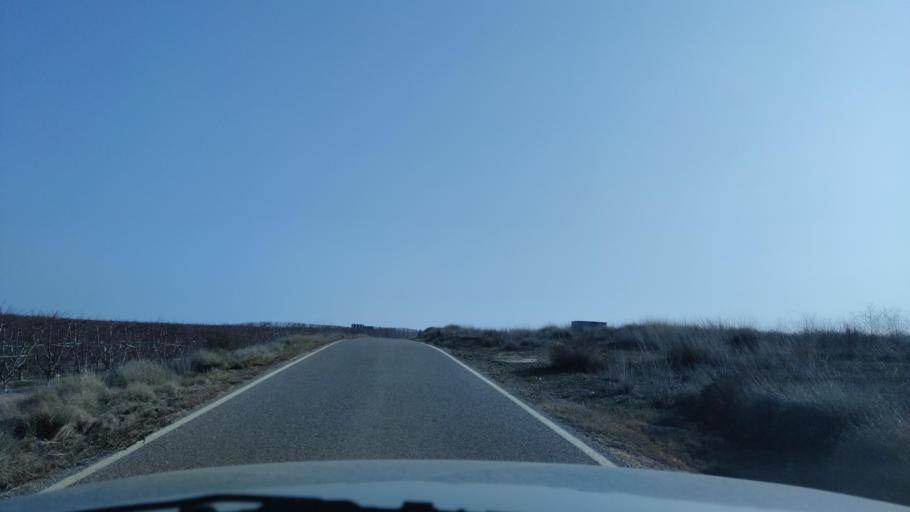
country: ES
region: Catalonia
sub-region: Provincia de Lleida
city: Sunyer
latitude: 41.5300
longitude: 0.5784
